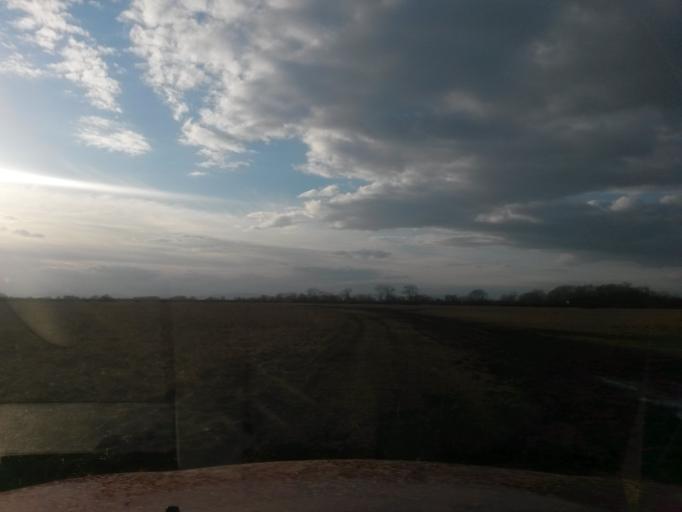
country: SK
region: Kosicky
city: Sobrance
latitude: 48.7047
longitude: 22.0920
